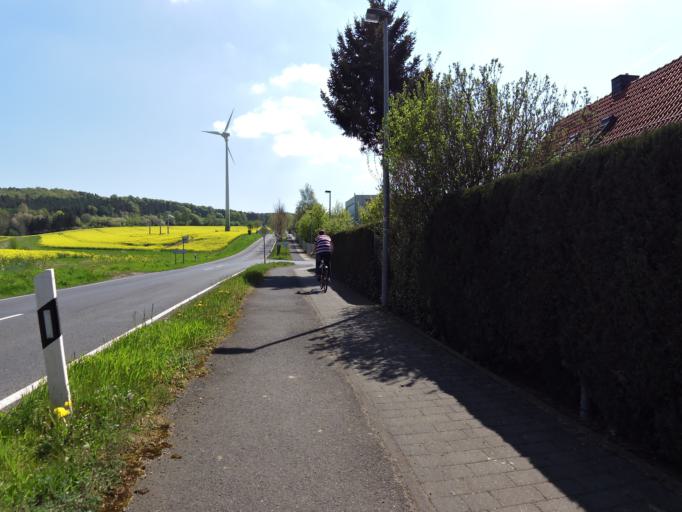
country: DE
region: Thuringia
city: Marksuhl
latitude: 50.9103
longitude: 10.2158
